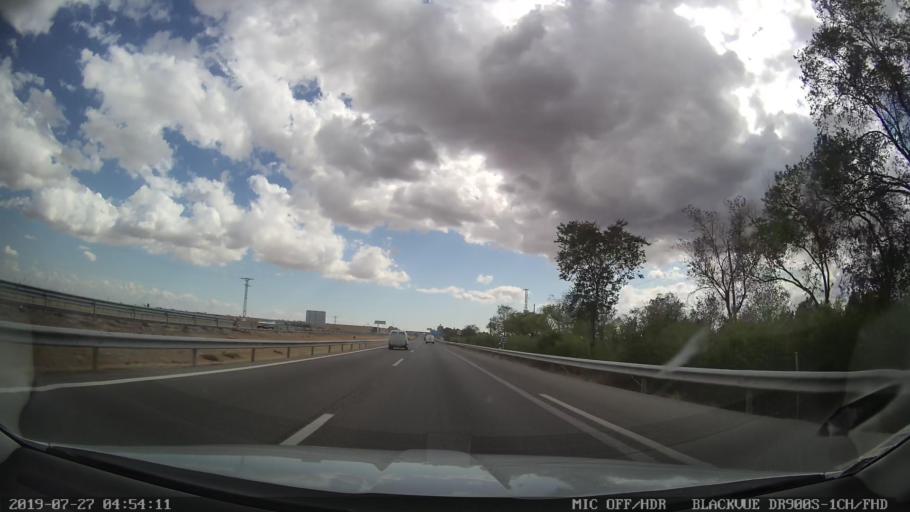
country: ES
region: Madrid
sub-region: Provincia de Madrid
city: Navalcarnero
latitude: 40.2758
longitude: -4.0301
